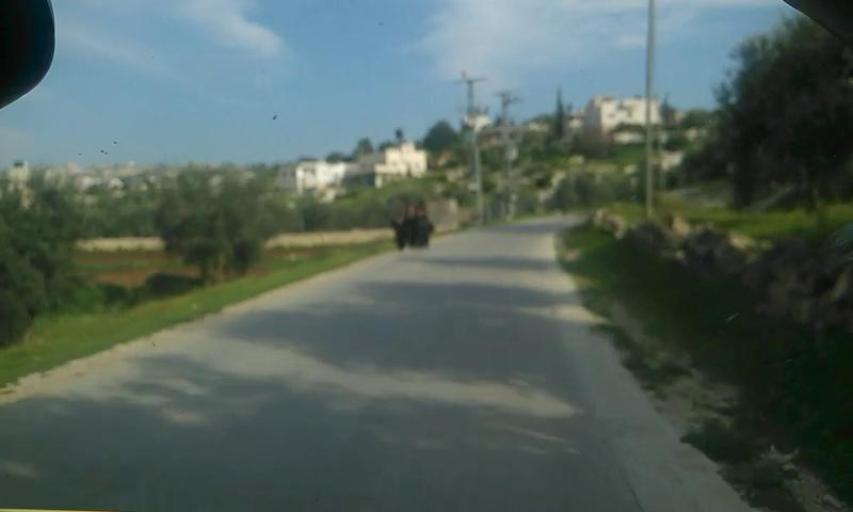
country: PS
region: West Bank
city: Nuba
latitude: 31.6131
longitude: 35.0339
